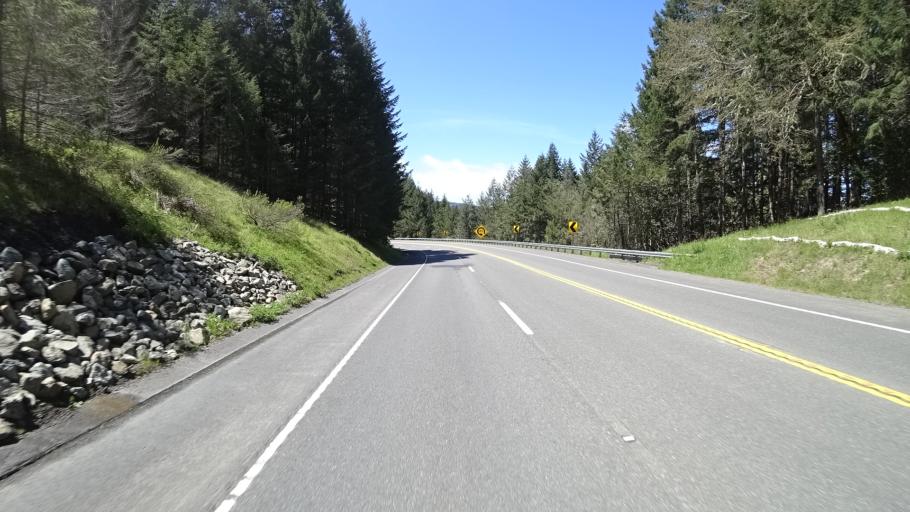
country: US
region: California
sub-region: Humboldt County
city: Willow Creek
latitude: 40.9259
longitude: -123.8086
